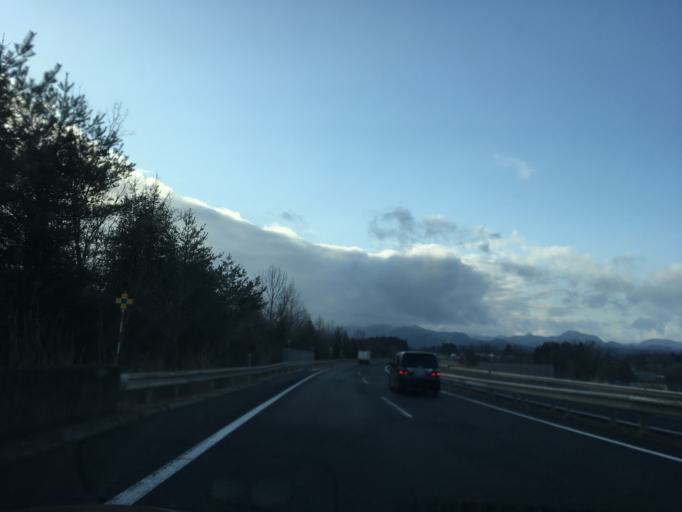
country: JP
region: Miyagi
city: Okawara
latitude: 38.1663
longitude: 140.6414
